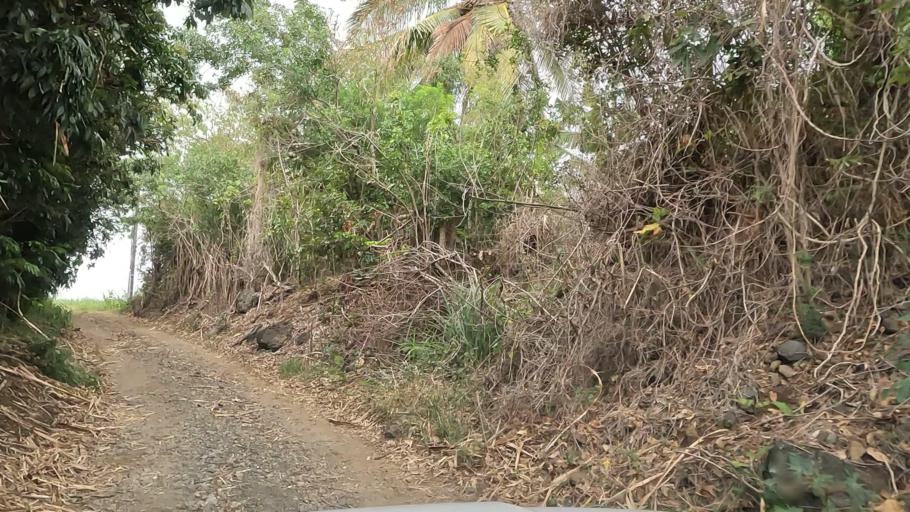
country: RE
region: Reunion
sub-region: Reunion
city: Saint-Pierre
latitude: -21.3384
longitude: 55.5225
